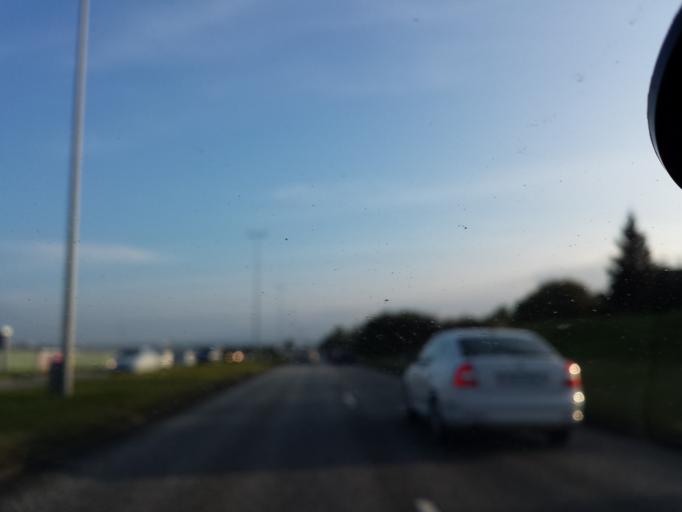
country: IS
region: Capital Region
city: Reykjavik
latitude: 64.1389
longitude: -21.8504
